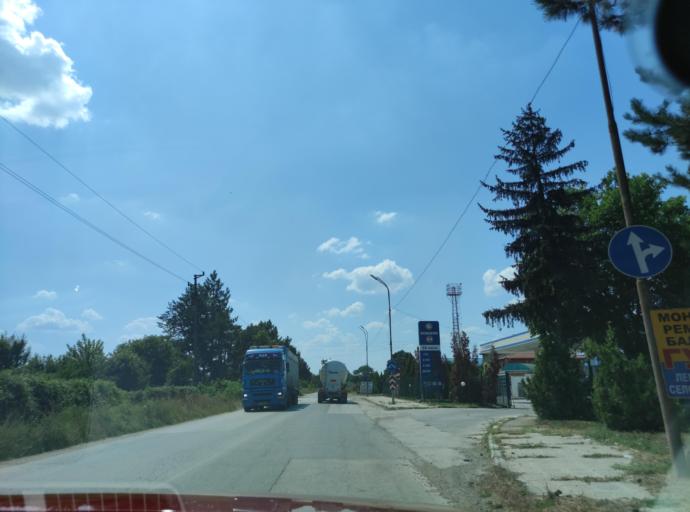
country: BG
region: Pleven
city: Iskur
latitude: 43.4534
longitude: 24.2520
